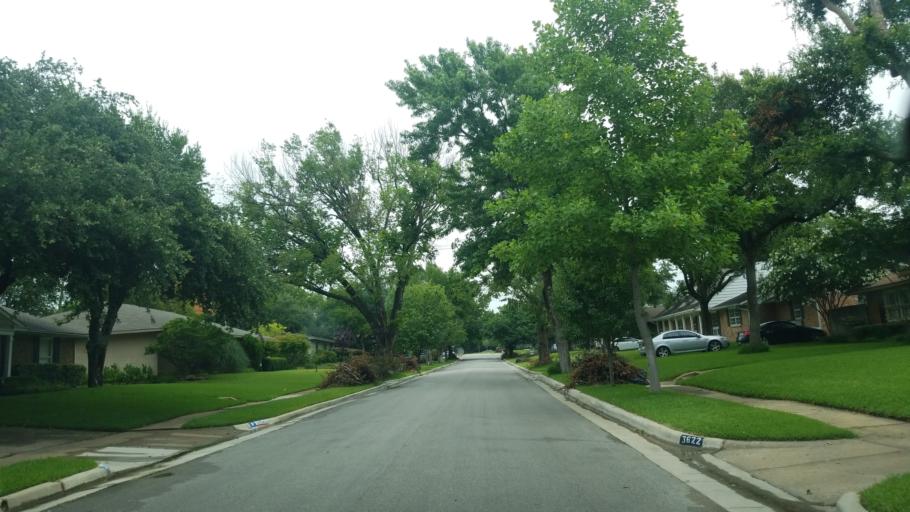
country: US
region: Texas
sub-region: Dallas County
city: Farmers Branch
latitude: 32.9032
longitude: -96.8579
